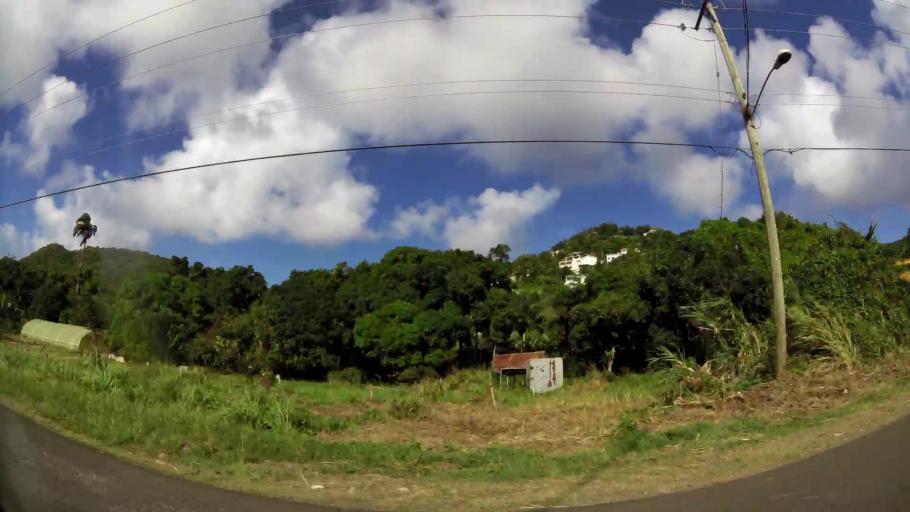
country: LC
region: Castries Quarter
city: Bisee
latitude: 14.0417
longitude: -60.9564
